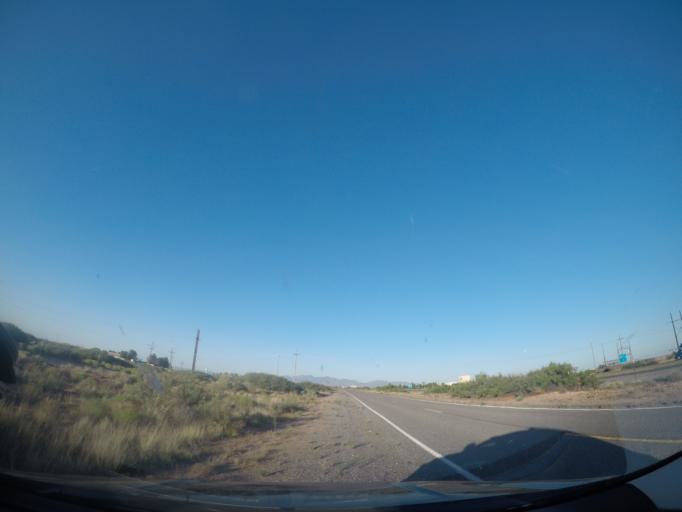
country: US
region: New Mexico
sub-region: Dona Ana County
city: Mesilla
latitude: 32.2705
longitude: -106.9402
